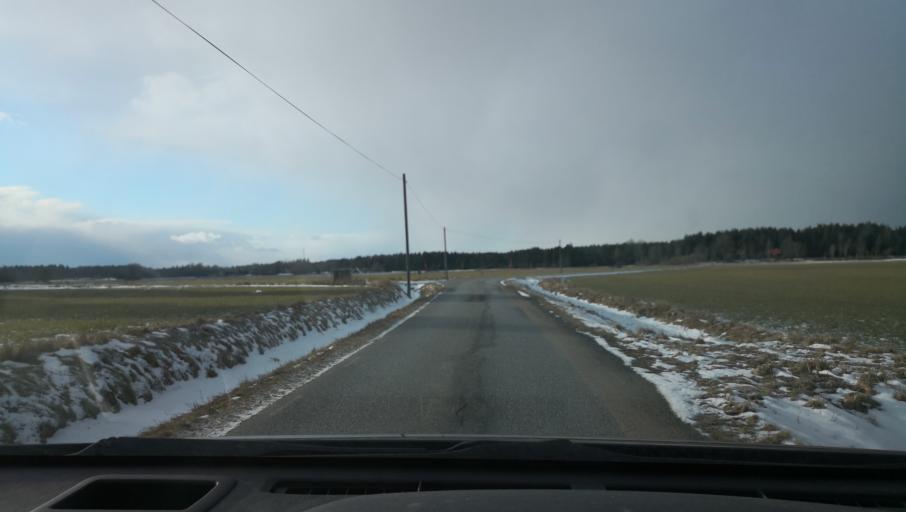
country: SE
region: Uppsala
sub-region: Enkopings Kommun
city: Irsta
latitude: 59.7055
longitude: 16.9184
